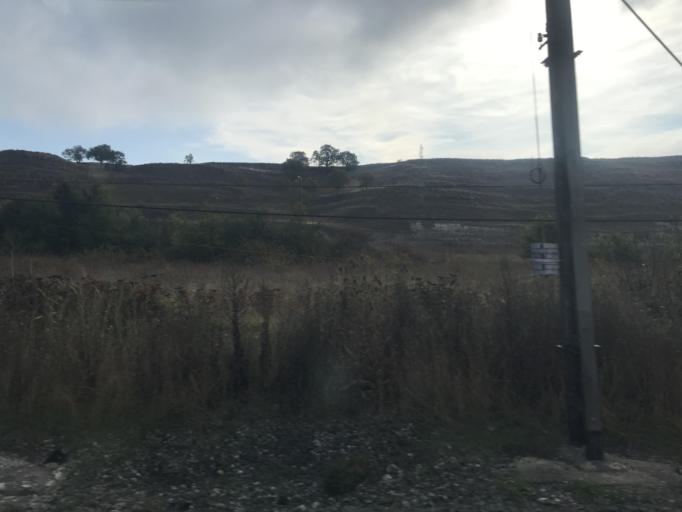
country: ES
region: Castille and Leon
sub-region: Provincia de Burgos
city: Briviesca
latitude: 42.5386
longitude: -3.3194
